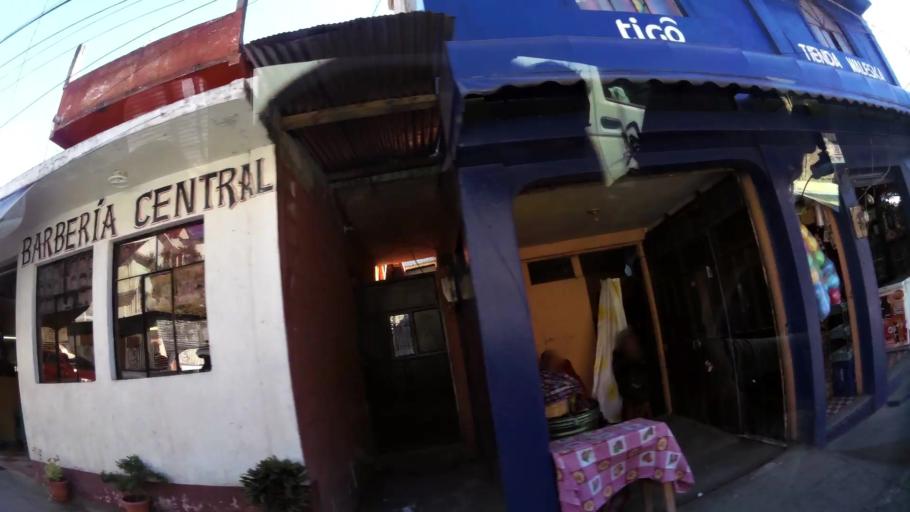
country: GT
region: Solola
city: Solola
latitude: 14.7773
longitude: -91.1838
